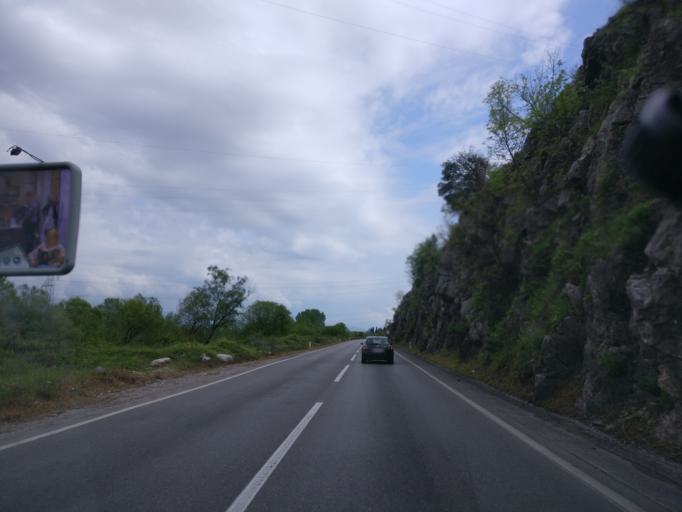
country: ME
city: Spuz
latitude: 42.4509
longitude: 19.1979
